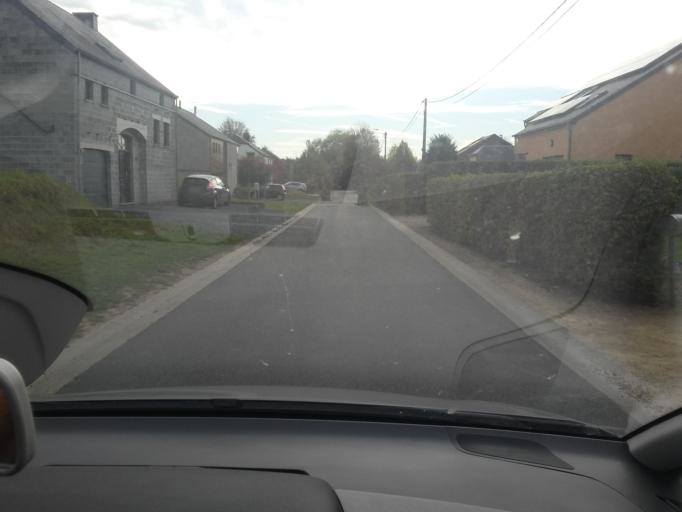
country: BE
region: Wallonia
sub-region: Province du Luxembourg
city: Attert
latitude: 49.7110
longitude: 5.7321
